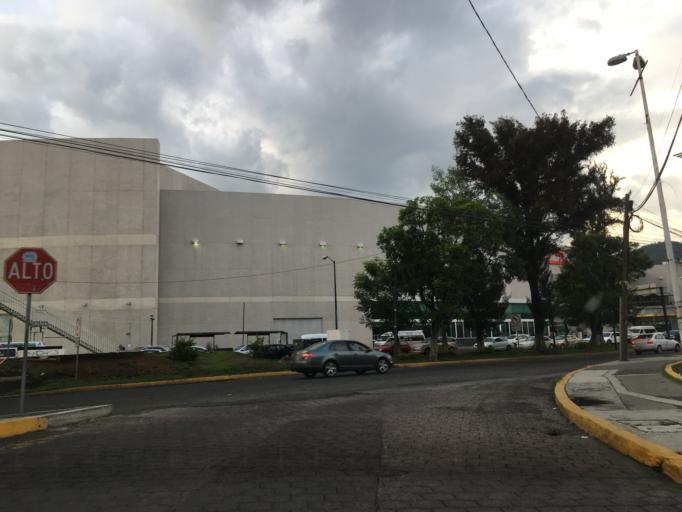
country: MX
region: Michoacan
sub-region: Morelia
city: Montana Monarca (Punta Altozano)
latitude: 19.6875
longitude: -101.1588
